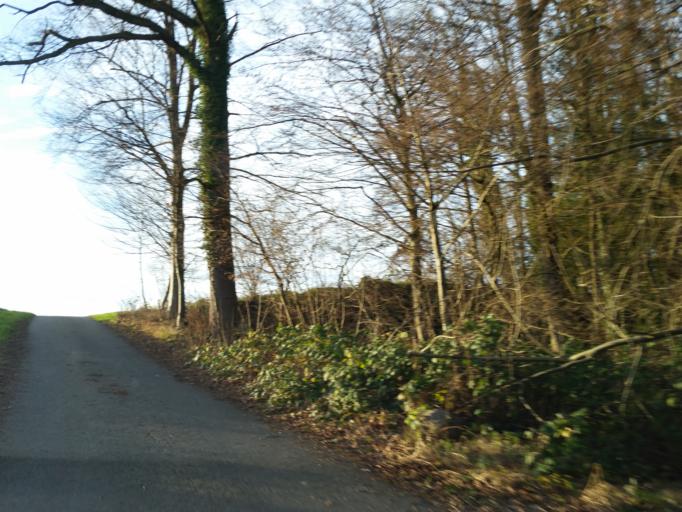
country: CH
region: Thurgau
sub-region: Arbon District
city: Amriswil
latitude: 47.5578
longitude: 9.3206
